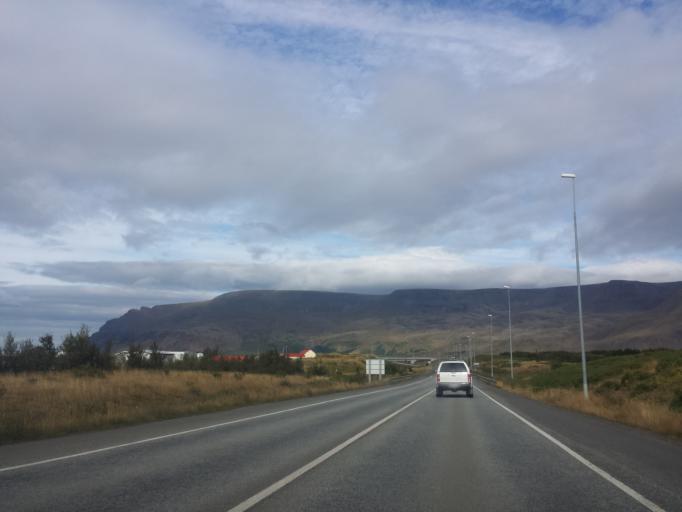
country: IS
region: Capital Region
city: Mosfellsbaer
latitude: 64.1787
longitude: -21.6778
